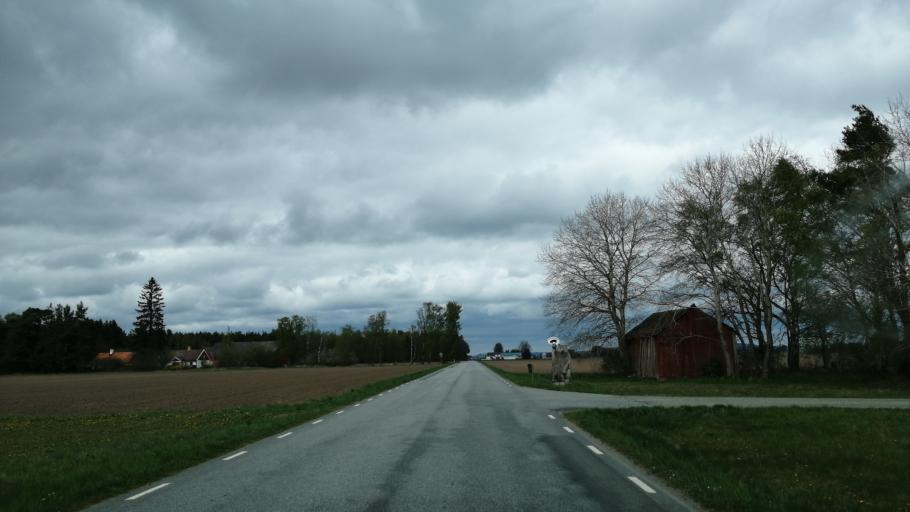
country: SE
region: Skane
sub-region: Kristianstads Kommun
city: Fjalkinge
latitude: 56.0501
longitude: 14.3343
